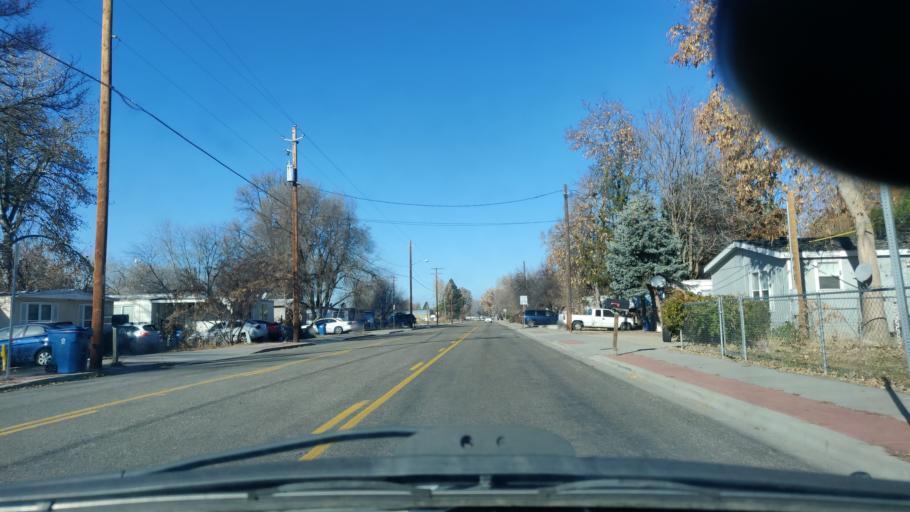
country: US
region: Idaho
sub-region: Ada County
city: Garden City
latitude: 43.6420
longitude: -116.2577
